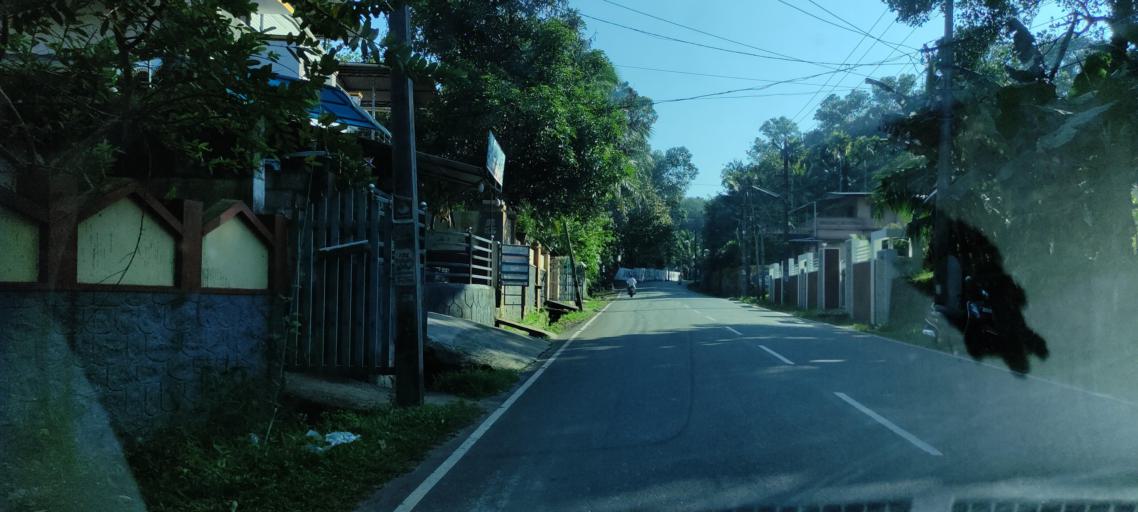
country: IN
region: Kerala
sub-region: Pattanamtitta
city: Pathanamthitta
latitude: 9.2246
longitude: 76.7526
